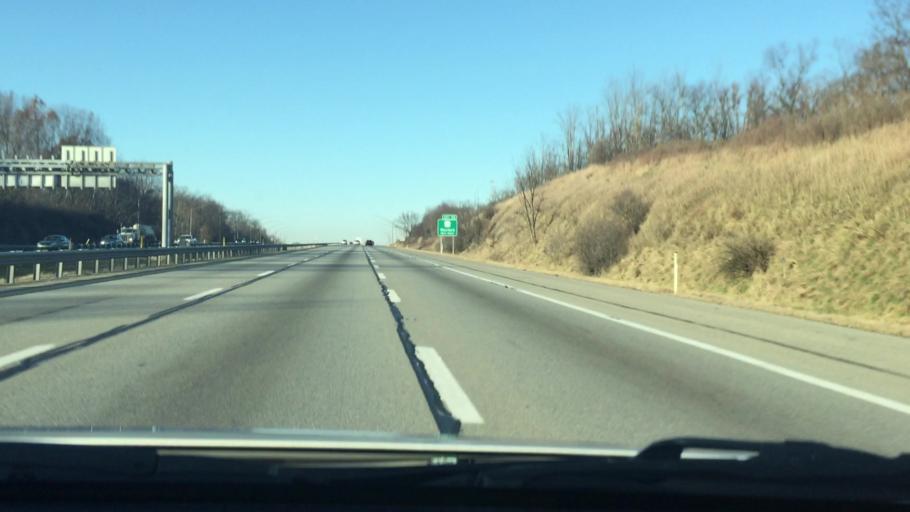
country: US
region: Pennsylvania
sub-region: Allegheny County
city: Franklin Park
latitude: 40.6059
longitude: -80.0941
